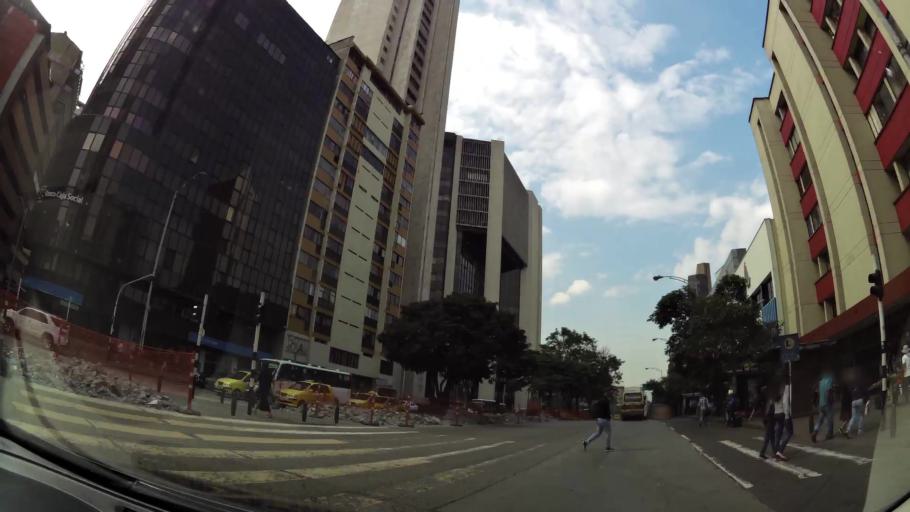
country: CO
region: Antioquia
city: Medellin
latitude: 6.2505
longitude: -75.5640
